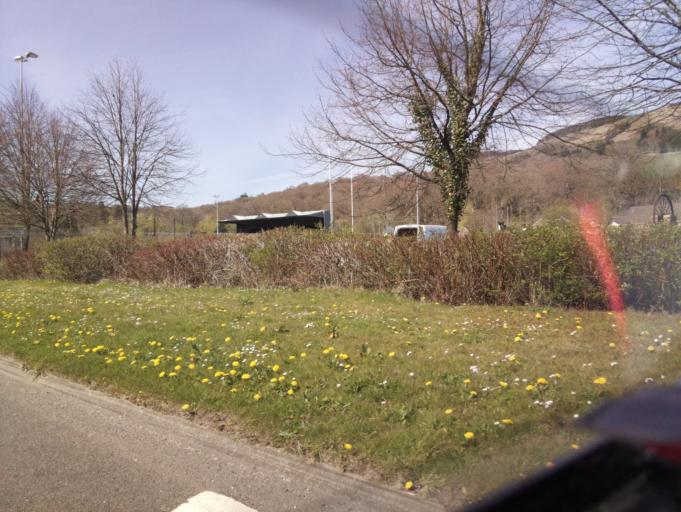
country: GB
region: Wales
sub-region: Rhondda Cynon Taf
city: Mountain Ash
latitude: 51.6861
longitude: -3.3827
